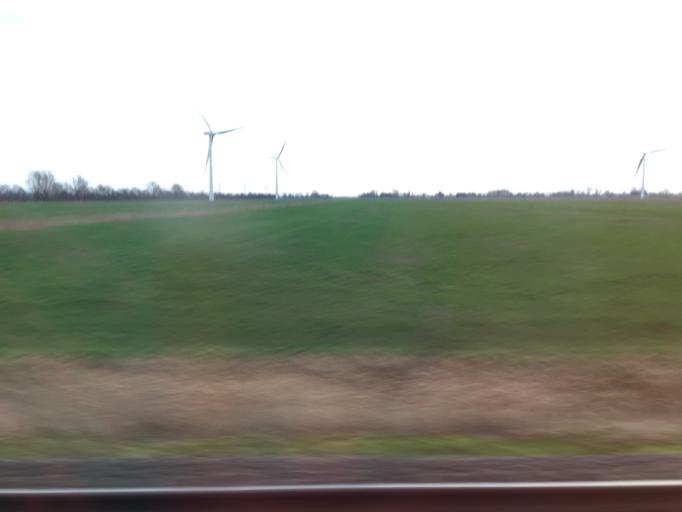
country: DE
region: Schleswig-Holstein
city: Krempdorf
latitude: 53.8222
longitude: 9.4688
